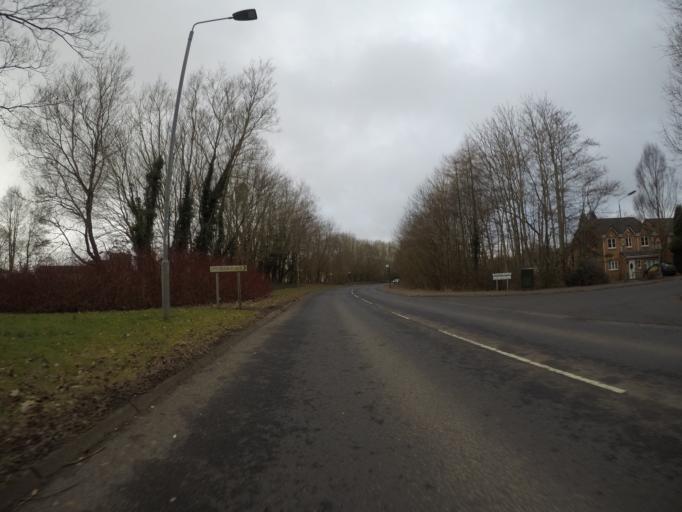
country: GB
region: Scotland
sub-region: North Ayrshire
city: Irvine
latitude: 55.6313
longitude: -4.6396
